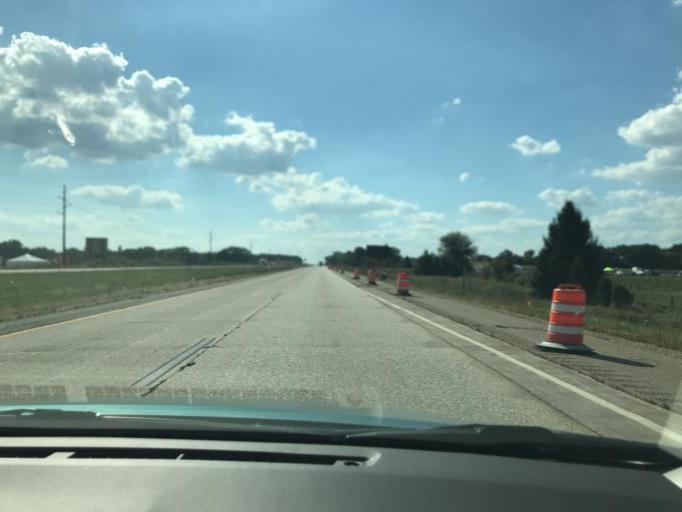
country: US
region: Wisconsin
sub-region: Walworth County
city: Darien
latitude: 42.6199
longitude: -88.6812
